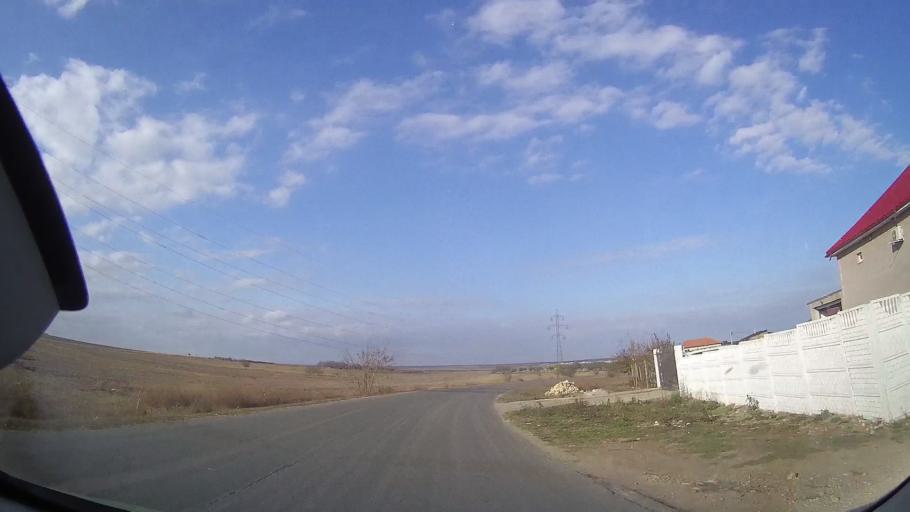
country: RO
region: Constanta
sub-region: Comuna Limanu
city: Limanu
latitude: 43.7955
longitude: 28.5203
